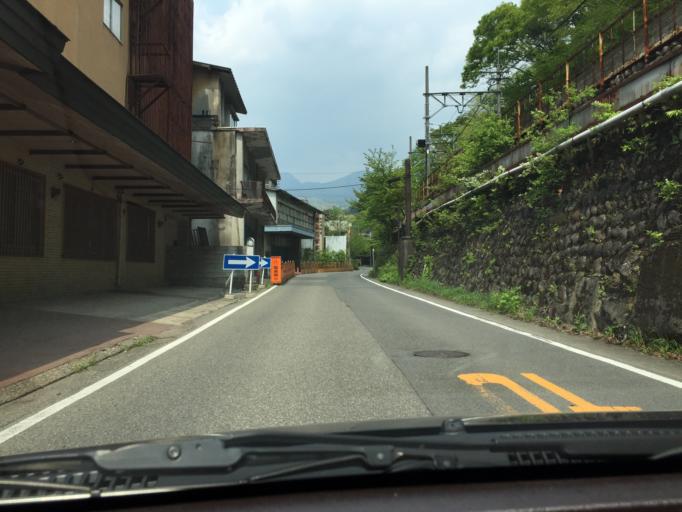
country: JP
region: Tochigi
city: Imaichi
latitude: 36.8358
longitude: 139.7213
